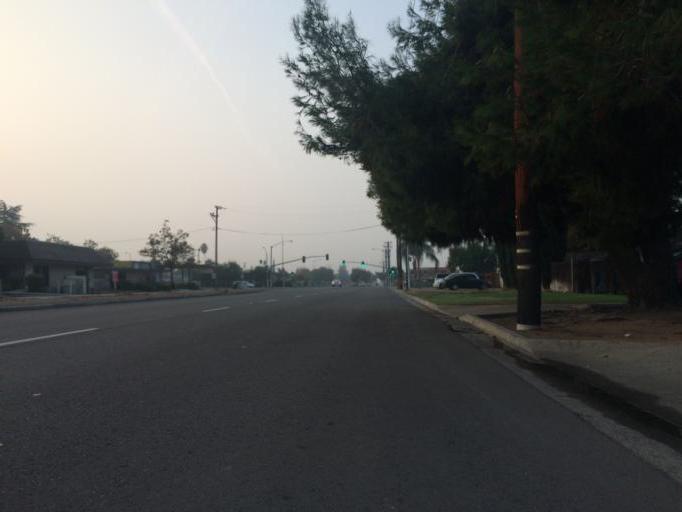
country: US
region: California
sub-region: Fresno County
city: Tarpey Village
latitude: 36.7735
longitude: -119.7364
